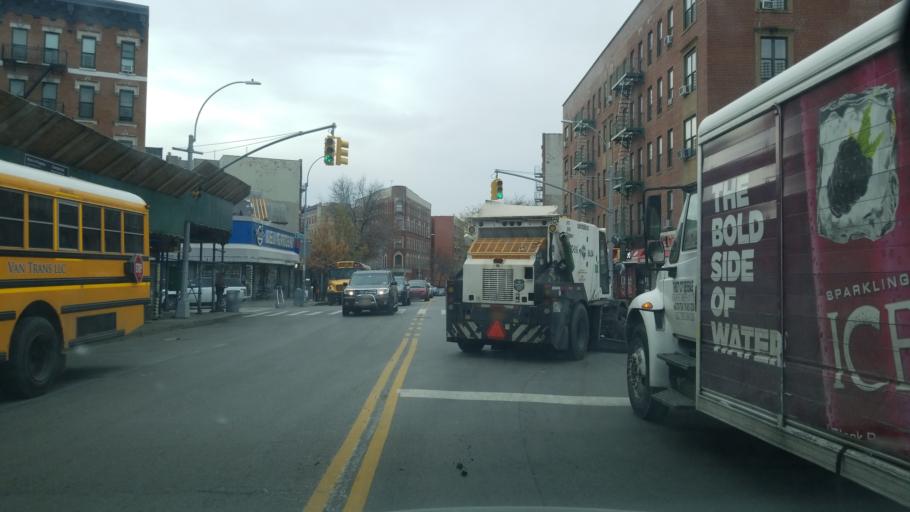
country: US
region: New York
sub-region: New York County
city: Inwood
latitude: 40.8274
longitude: -73.9048
